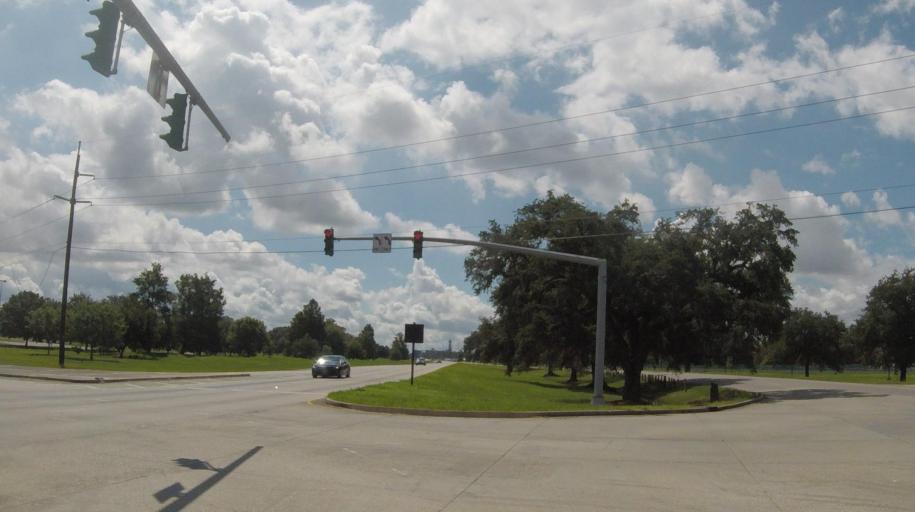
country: US
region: Louisiana
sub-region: West Baton Rouge Parish
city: Port Allen
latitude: 30.4085
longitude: -91.1861
